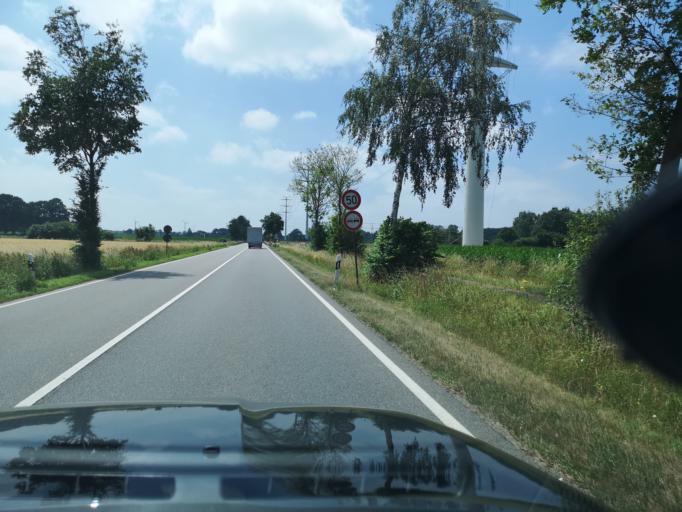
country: DE
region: North Rhine-Westphalia
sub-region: Regierungsbezirk Munster
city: Isselburg
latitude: 51.8330
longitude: 6.4510
